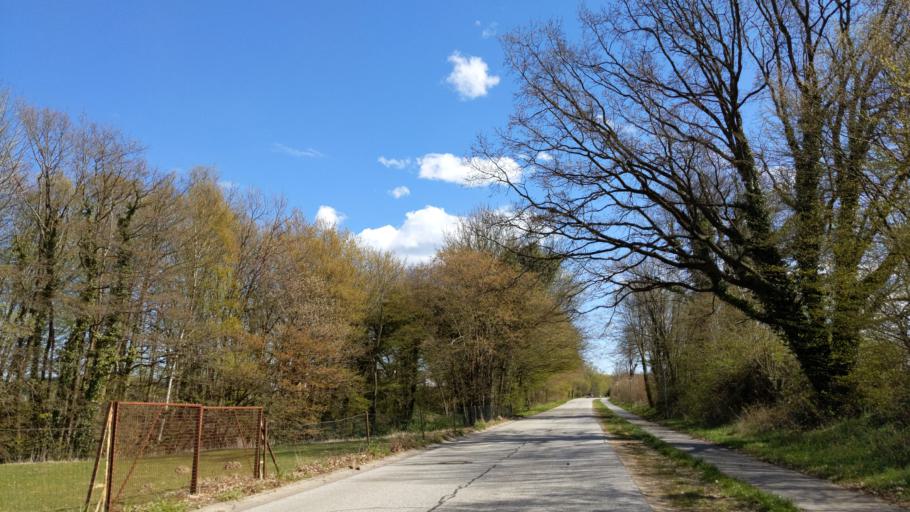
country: DE
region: Mecklenburg-Vorpommern
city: Selmsdorf
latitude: 53.8883
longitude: 10.8868
